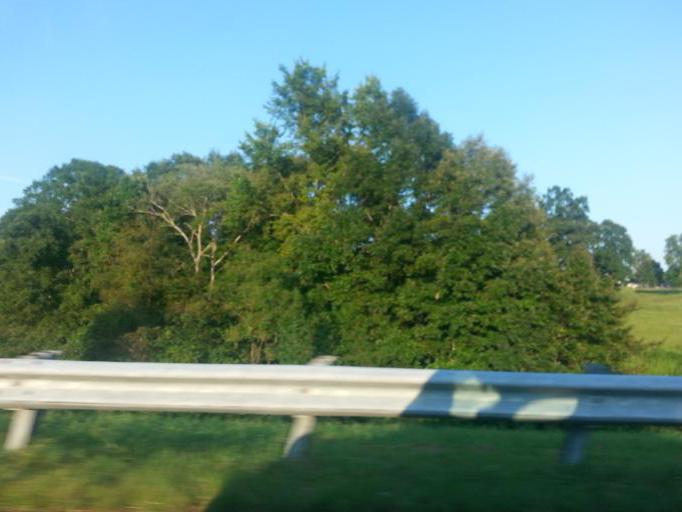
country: US
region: Tennessee
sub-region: Meigs County
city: Decatur
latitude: 35.5587
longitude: -84.6682
